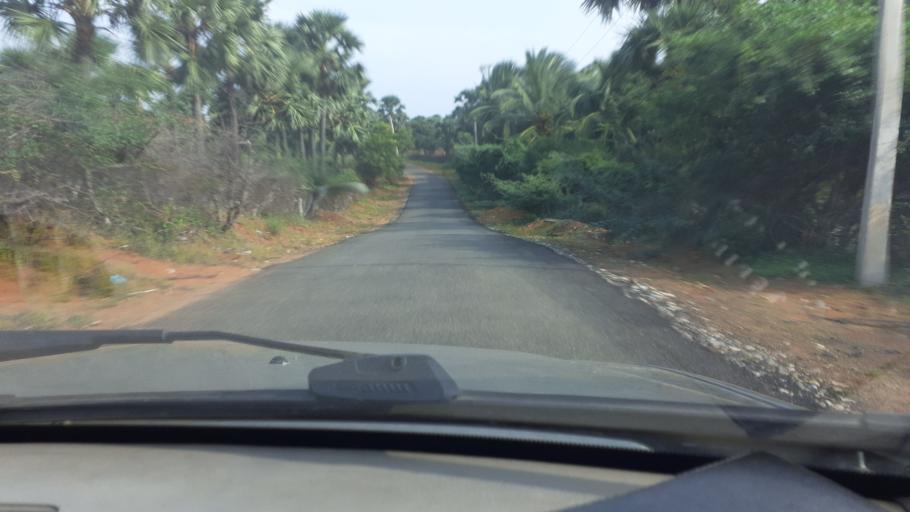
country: IN
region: Tamil Nadu
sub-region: Tirunelveli Kattabo
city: Tisaiyanvilai
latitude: 8.3370
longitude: 77.9481
